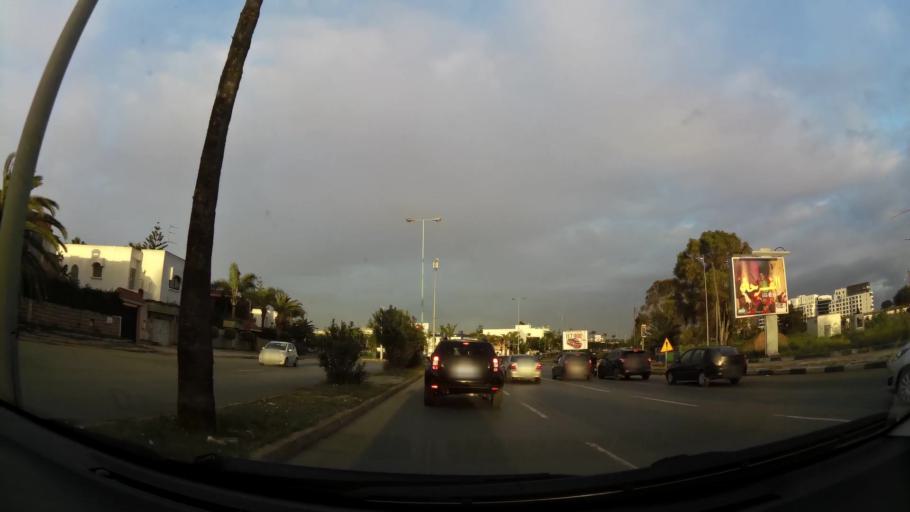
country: MA
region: Grand Casablanca
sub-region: Casablanca
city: Casablanca
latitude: 33.5699
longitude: -7.6631
